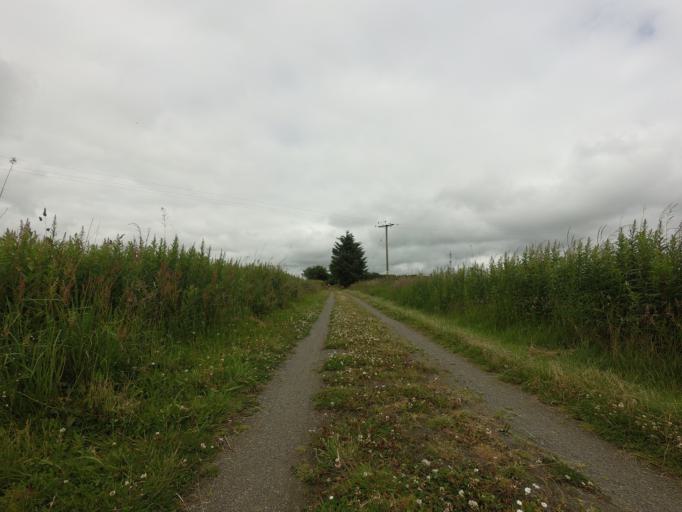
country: GB
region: Scotland
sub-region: Aberdeenshire
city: Mintlaw
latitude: 57.4884
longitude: -2.1348
